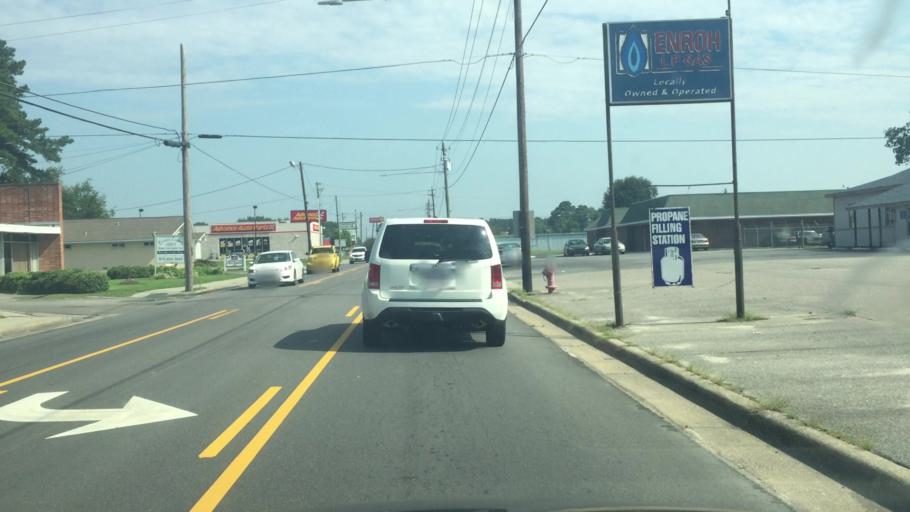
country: US
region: North Carolina
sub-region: Columbus County
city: Chadbourn
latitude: 34.3285
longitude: -78.8264
